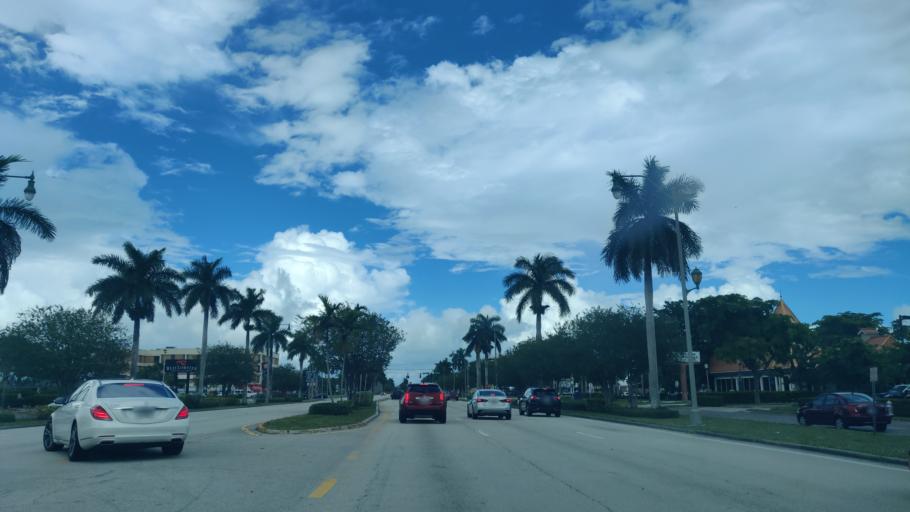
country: US
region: Florida
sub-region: Palm Beach County
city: Schall Circle
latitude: 26.7105
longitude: -80.0971
